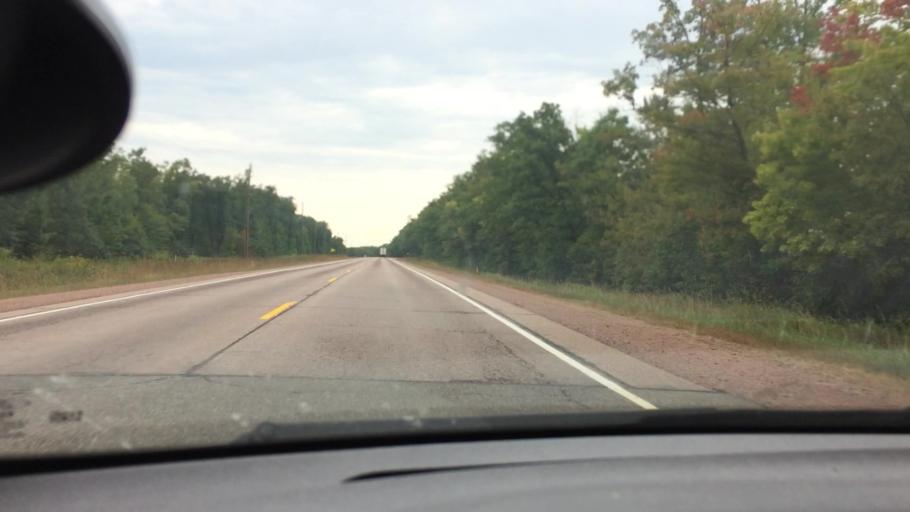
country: US
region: Wisconsin
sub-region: Clark County
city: Neillsville
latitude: 44.5787
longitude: -90.7382
